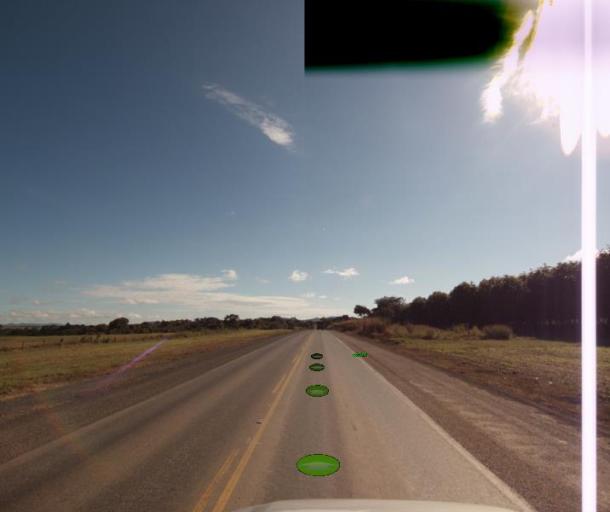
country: BR
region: Goias
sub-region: Uruacu
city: Uruacu
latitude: -14.6435
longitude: -49.1819
